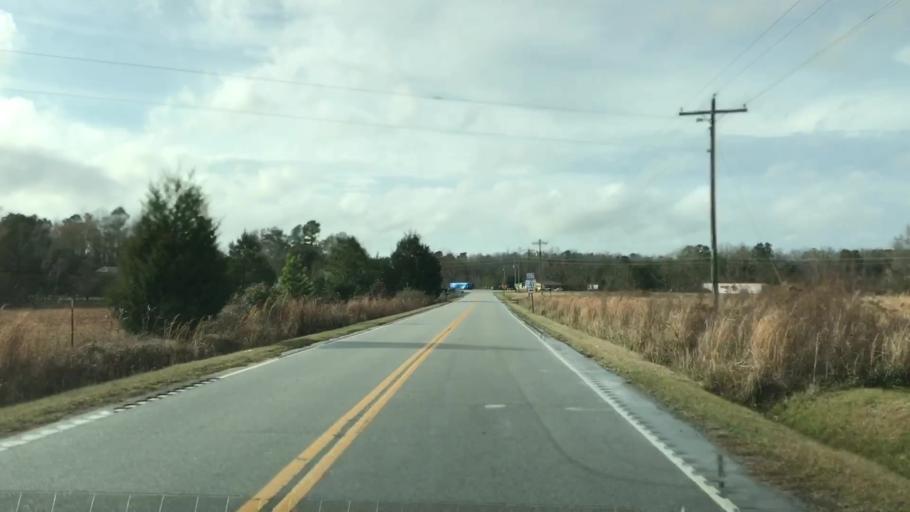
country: US
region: South Carolina
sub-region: Williamsburg County
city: Andrews
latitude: 33.5025
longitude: -79.5217
